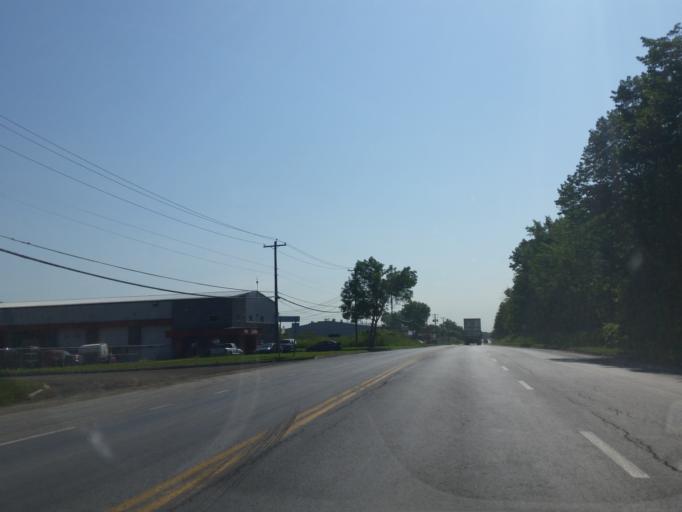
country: CA
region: Quebec
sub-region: Monteregie
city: Saint-Jean-sur-Richelieu
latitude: 45.3036
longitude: -73.3109
